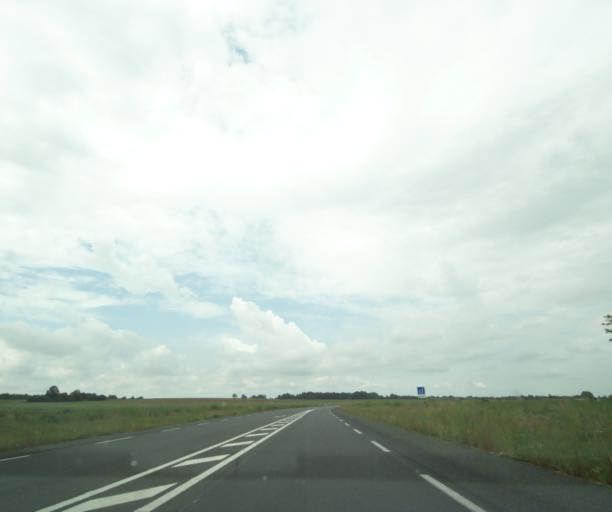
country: FR
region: Poitou-Charentes
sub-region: Departement des Deux-Sevres
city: Louzy
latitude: 47.0510
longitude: -0.1961
